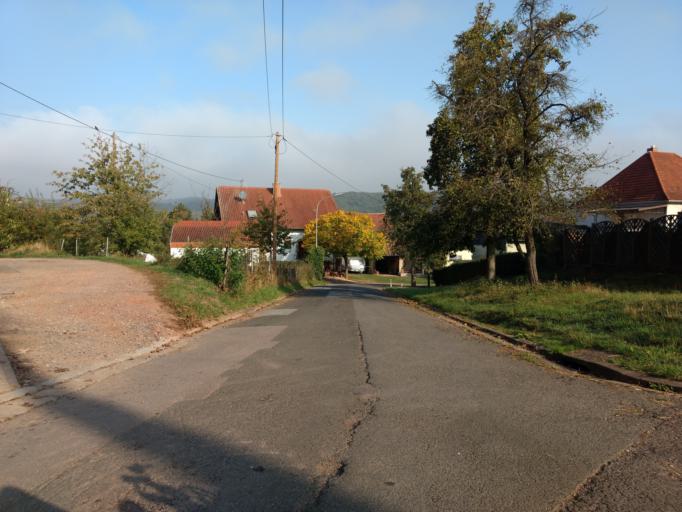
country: DE
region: Saarland
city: Saarwellingen
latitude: 49.3840
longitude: 6.8250
